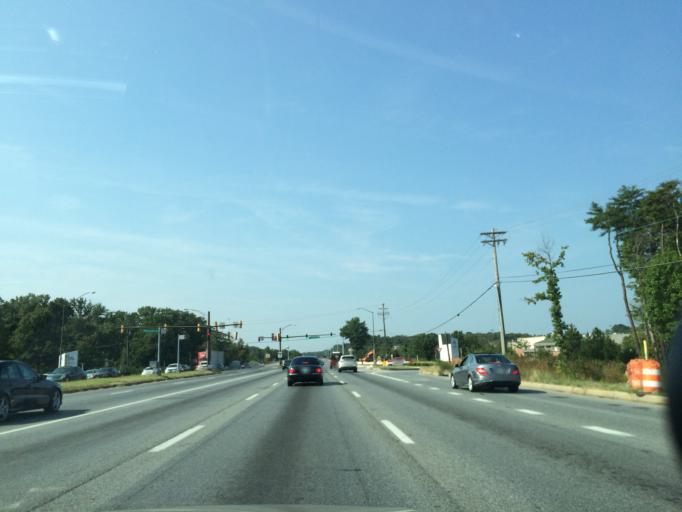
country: US
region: Maryland
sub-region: Charles County
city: Saint Charles
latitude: 38.6125
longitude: -76.9249
